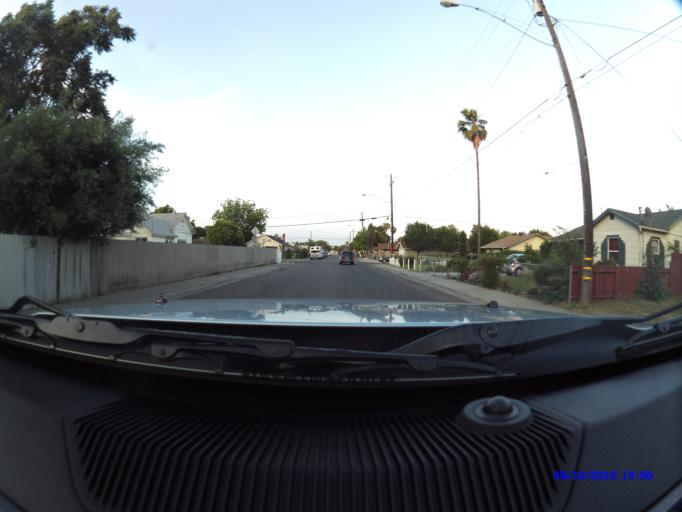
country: US
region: California
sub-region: San Joaquin County
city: Garden Acres
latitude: 37.9527
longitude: -121.2456
